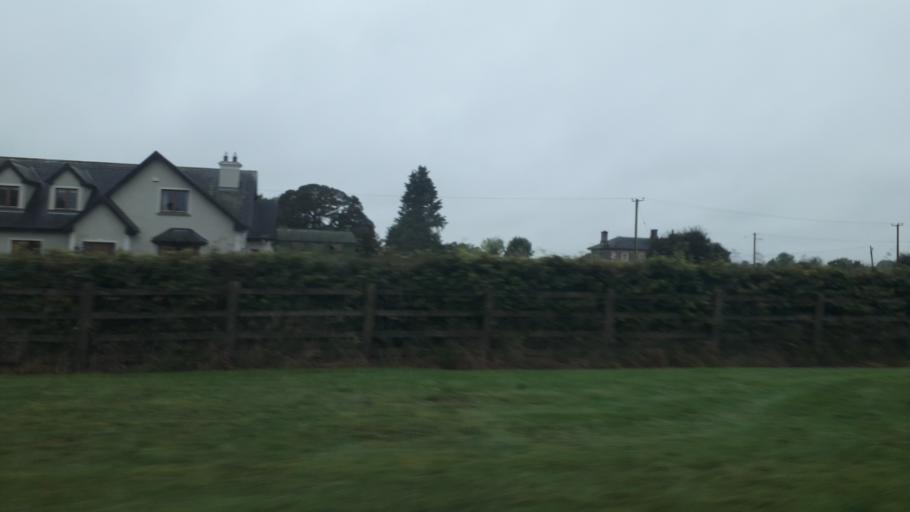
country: IE
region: Leinster
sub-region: An Longfort
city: Edgeworthstown
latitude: 53.6895
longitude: -7.6013
